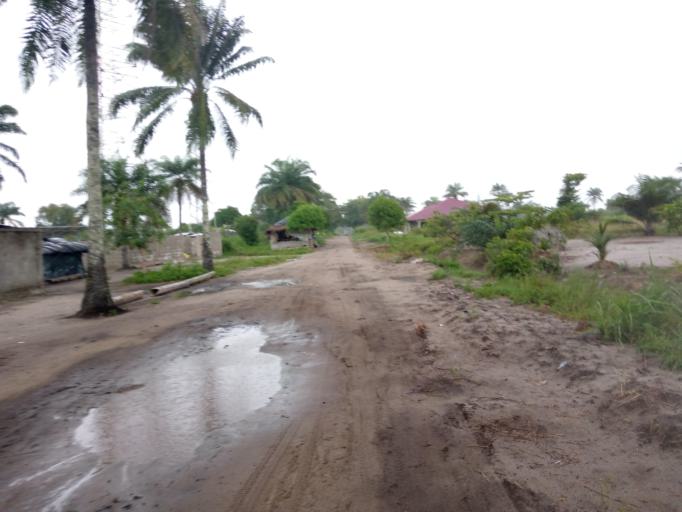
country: SL
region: Southern Province
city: Bonthe
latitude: 7.5273
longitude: -12.5134
